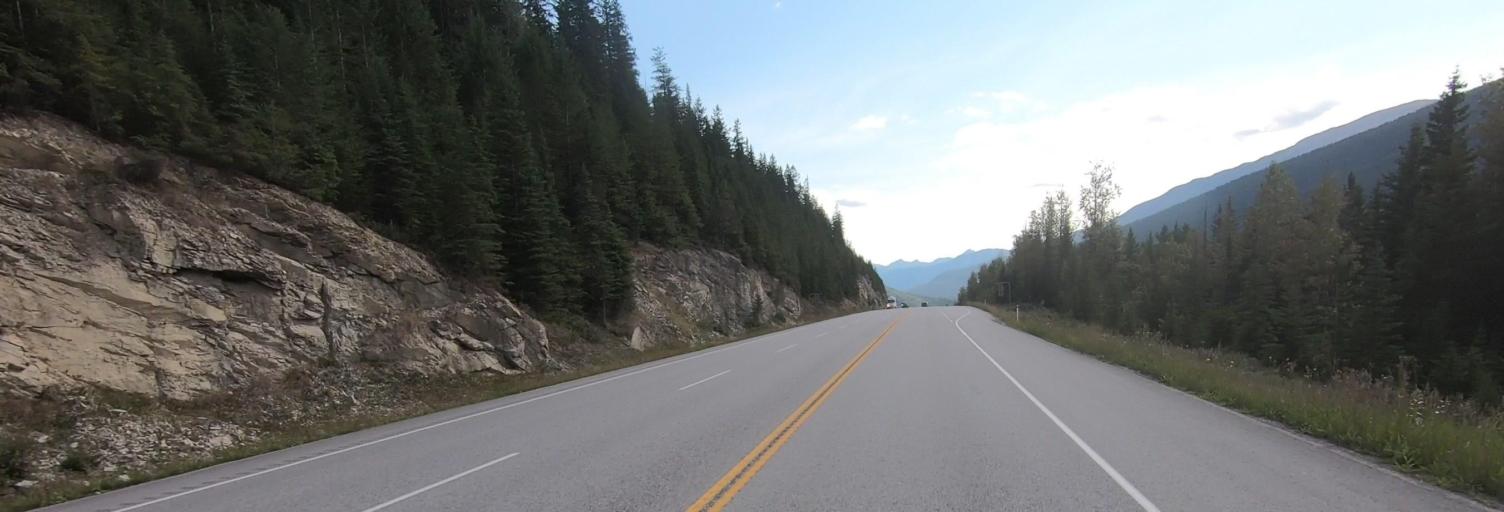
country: CA
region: Alberta
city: Lake Louise
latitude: 51.3178
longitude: -116.5766
